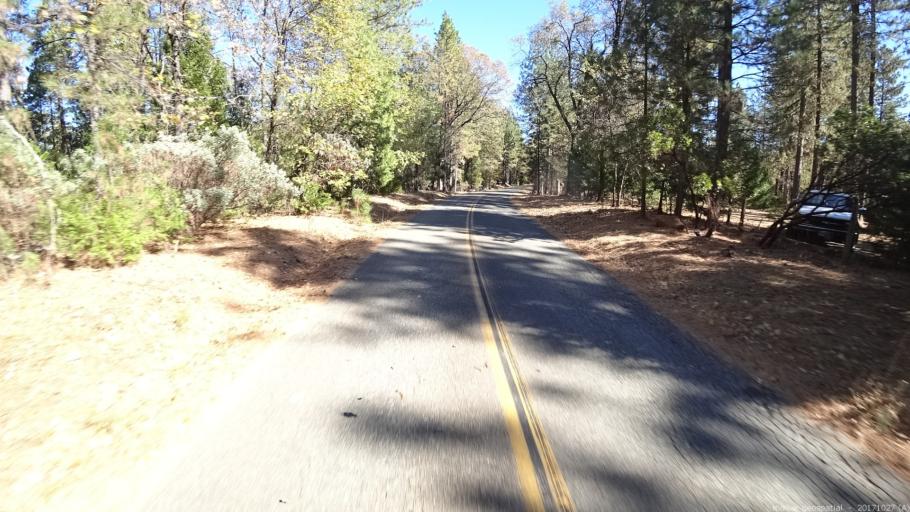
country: US
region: California
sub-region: Shasta County
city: Bella Vista
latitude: 40.7215
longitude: -122.0150
